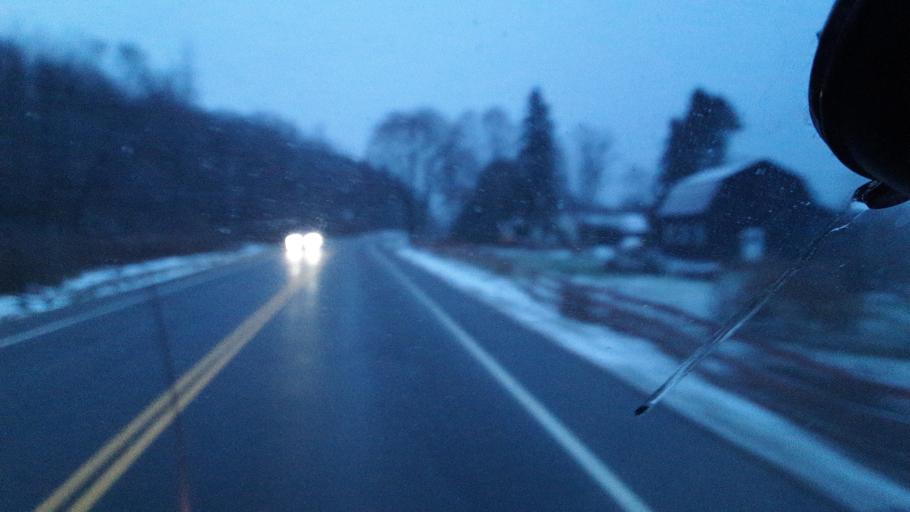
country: US
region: New York
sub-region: Allegany County
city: Belmont
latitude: 42.3117
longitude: -78.0962
